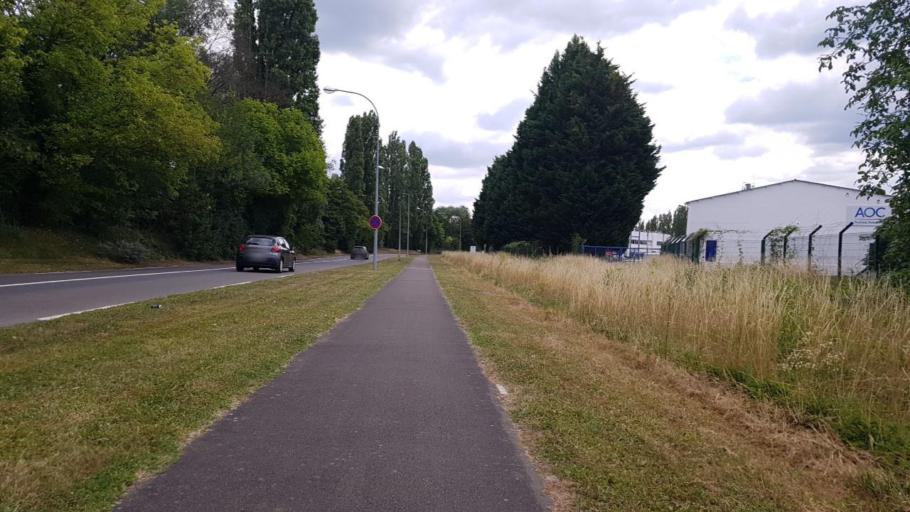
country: FR
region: Picardie
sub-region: Departement de l'Oise
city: Clairoix
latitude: 49.4338
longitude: 2.8485
